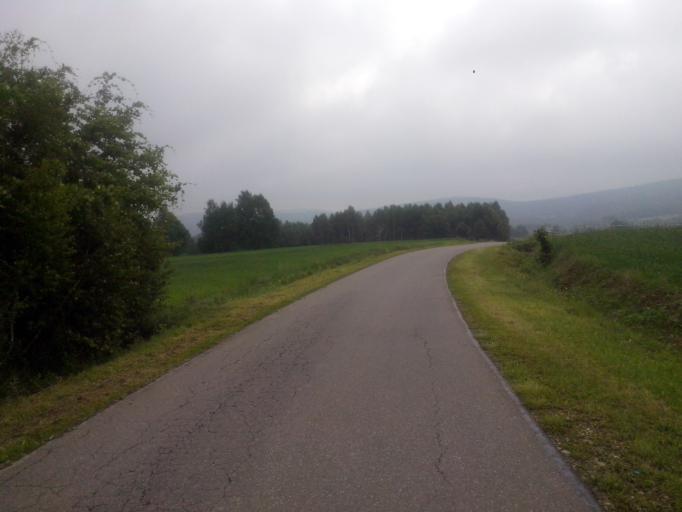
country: PL
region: Subcarpathian Voivodeship
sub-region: Powiat strzyzowski
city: Wysoka Strzyzowska
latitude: 49.8022
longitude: 21.7886
